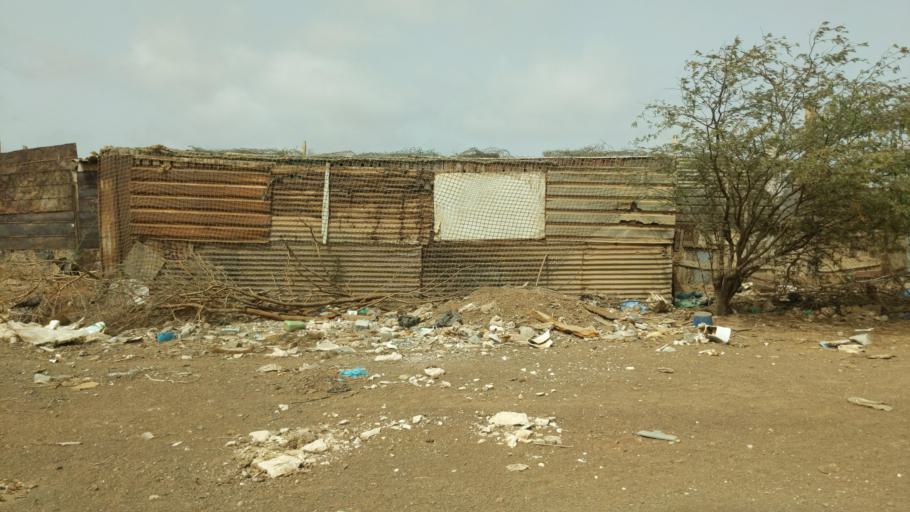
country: CV
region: Sal
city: Espargos
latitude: 16.7732
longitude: -22.9473
